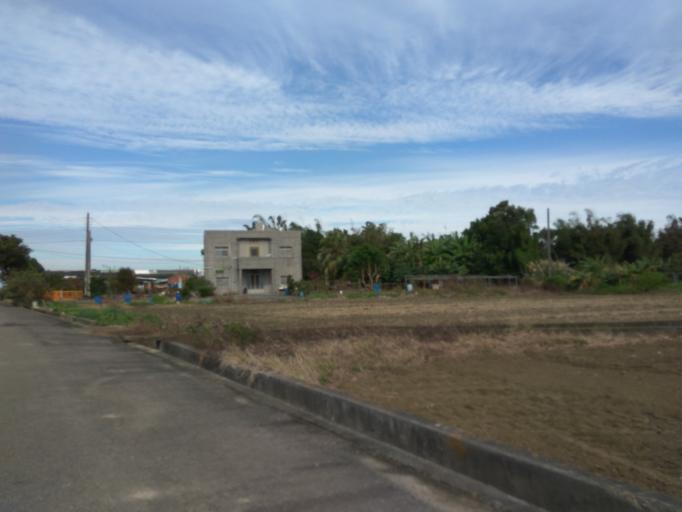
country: TW
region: Taiwan
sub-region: Hsinchu
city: Zhubei
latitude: 24.9857
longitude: 121.0895
